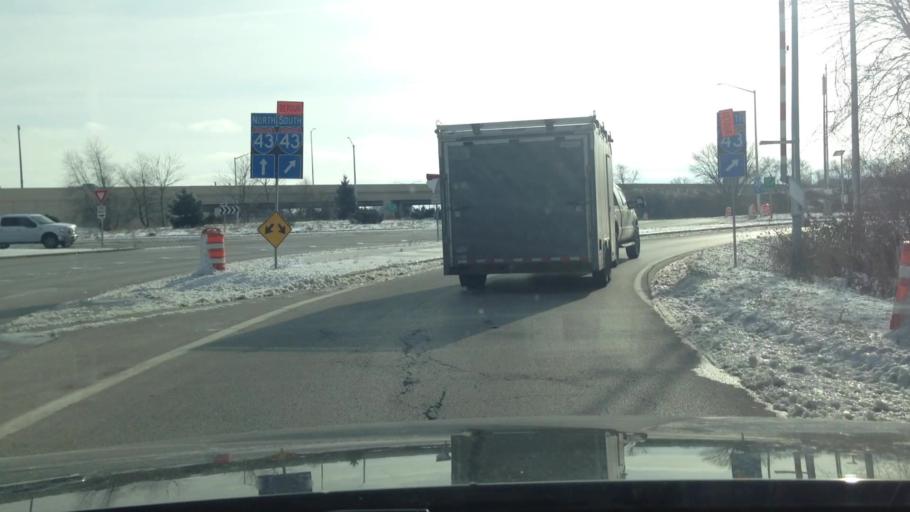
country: US
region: Wisconsin
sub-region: Waukesha County
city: New Berlin
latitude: 42.9542
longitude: -88.1091
